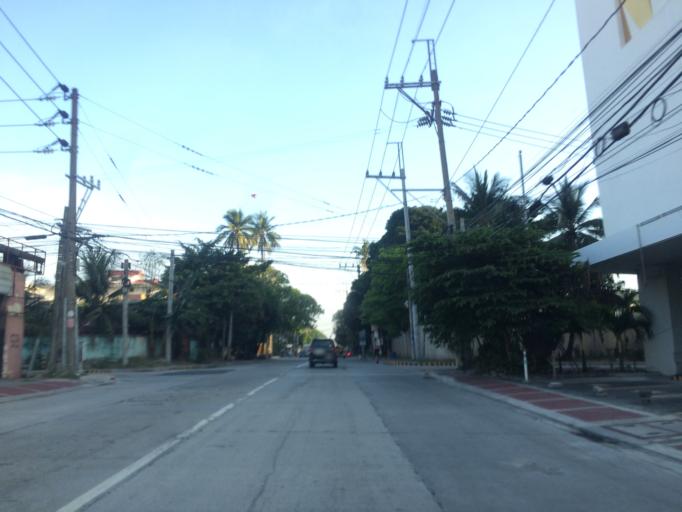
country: PH
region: Calabarzon
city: Del Monte
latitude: 14.6219
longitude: 121.0034
